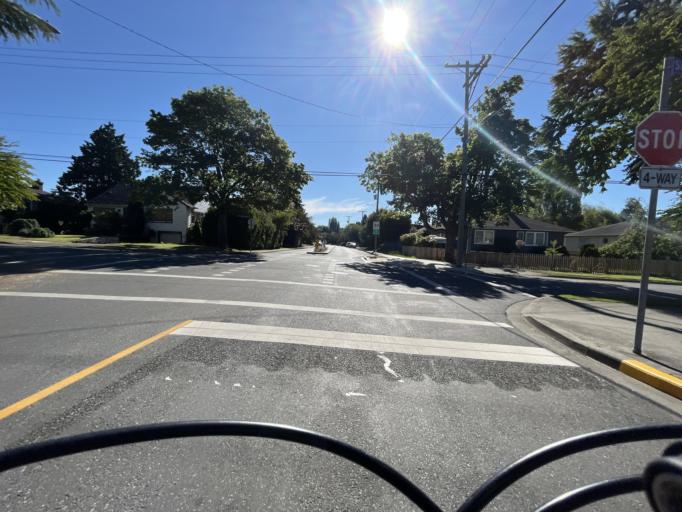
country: CA
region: British Columbia
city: Victoria
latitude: 48.4162
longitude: -123.3377
